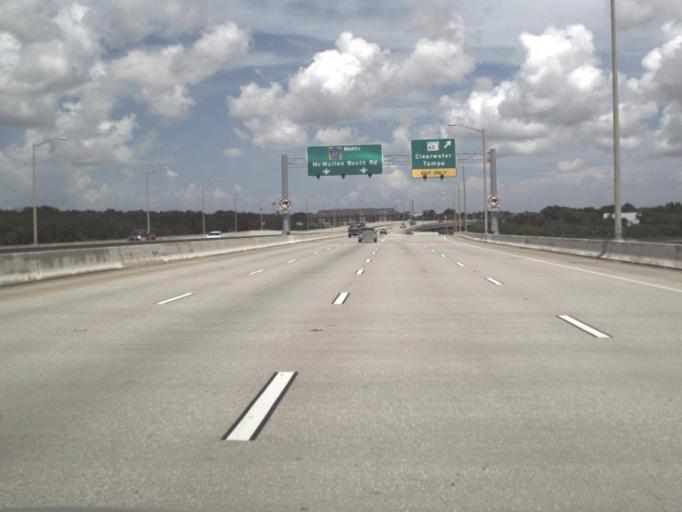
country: US
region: Florida
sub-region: Pinellas County
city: South Highpoint
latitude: 27.9551
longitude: -82.7077
